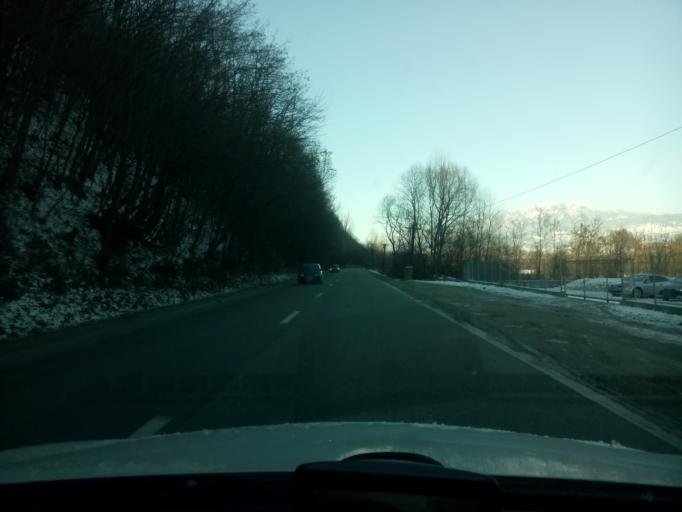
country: RO
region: Valcea
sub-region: Comuna Daesti
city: Daesti
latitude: 45.2041
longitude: 24.3735
